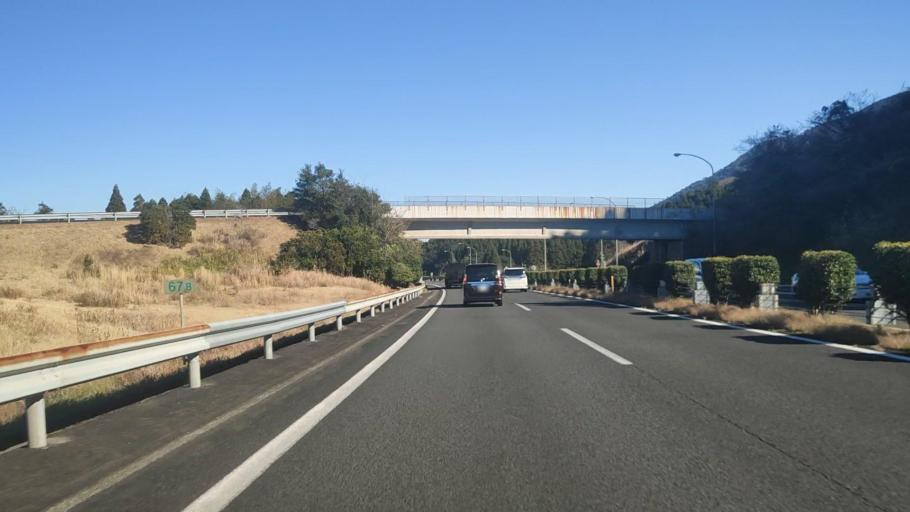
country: JP
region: Miyazaki
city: Miyazaki-shi
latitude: 31.8213
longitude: 131.3021
